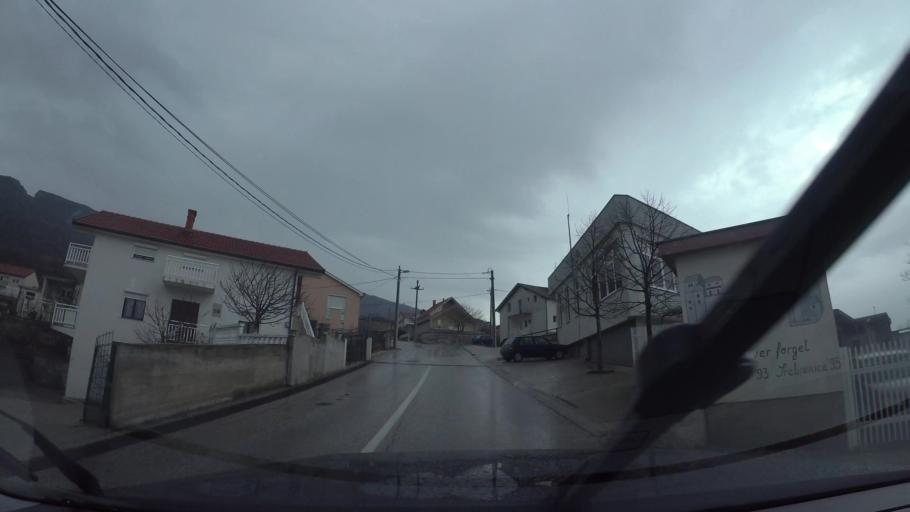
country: BA
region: Federation of Bosnia and Herzegovina
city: Rodoc
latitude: 43.3174
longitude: 17.8359
